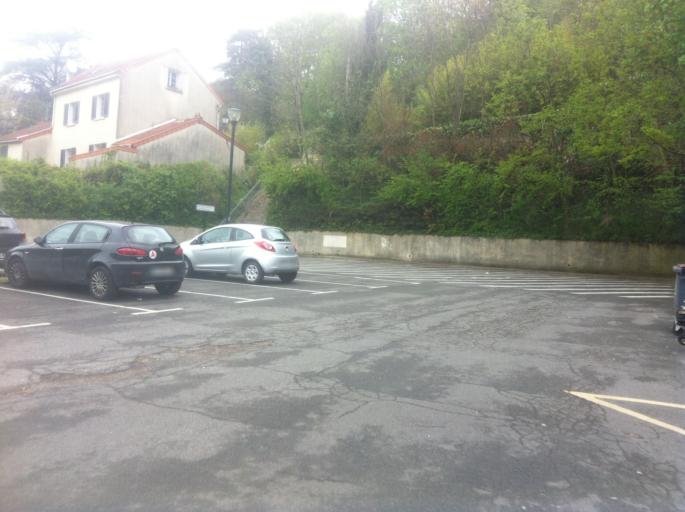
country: FR
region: Ile-de-France
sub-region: Departement du Val-d'Oise
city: Auvers-sur-Oise
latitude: 49.0718
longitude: 2.1705
